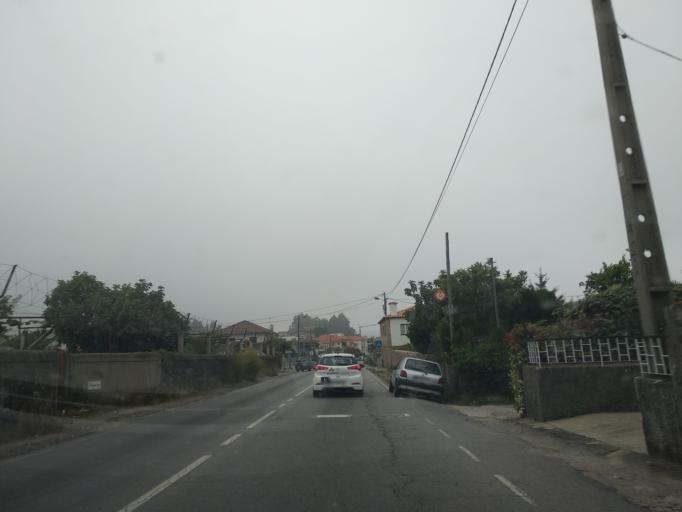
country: PT
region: Braga
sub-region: Vila Verde
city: Vila Verde
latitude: 41.6320
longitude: -8.4337
